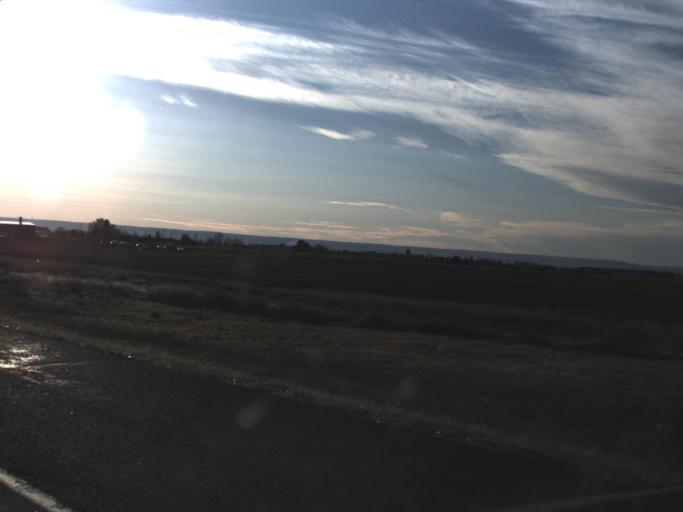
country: US
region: Washington
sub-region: Walla Walla County
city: Walla Walla East
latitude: 46.0982
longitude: -118.2540
